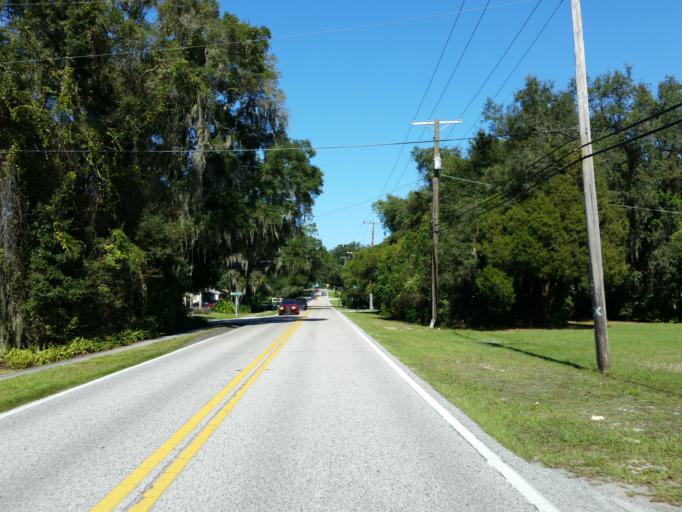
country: US
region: Florida
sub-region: Hillsborough County
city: Bloomingdale
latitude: 27.9029
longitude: -82.2692
